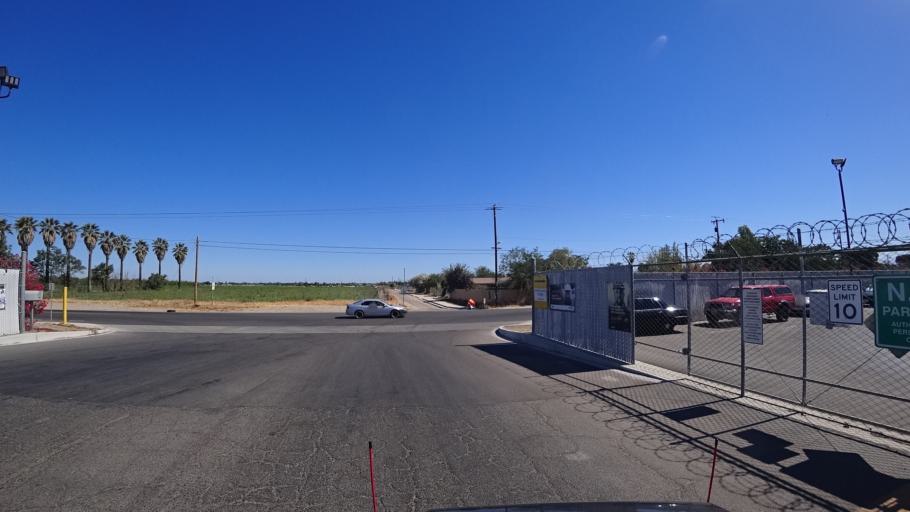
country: US
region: California
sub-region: Fresno County
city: Easton
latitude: 36.6920
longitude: -119.8021
